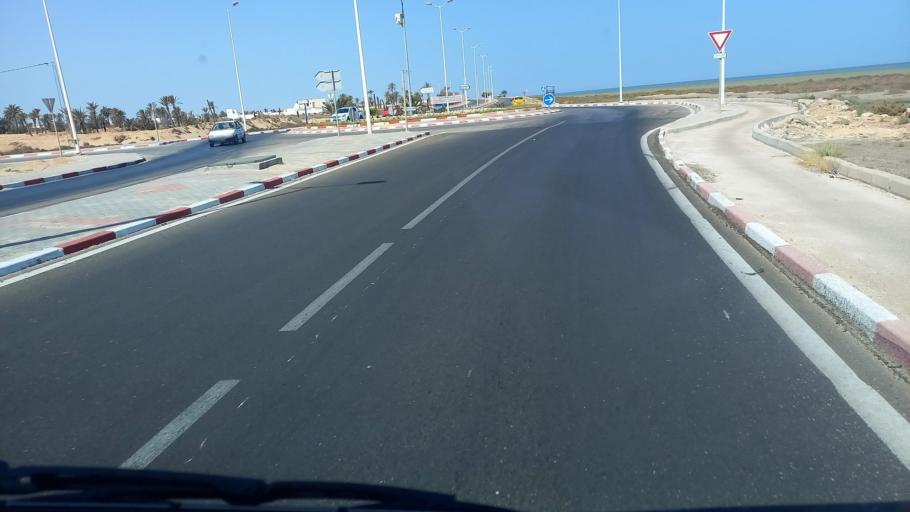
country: TN
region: Madanin
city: Houmt Souk
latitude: 33.8734
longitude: 10.9297
